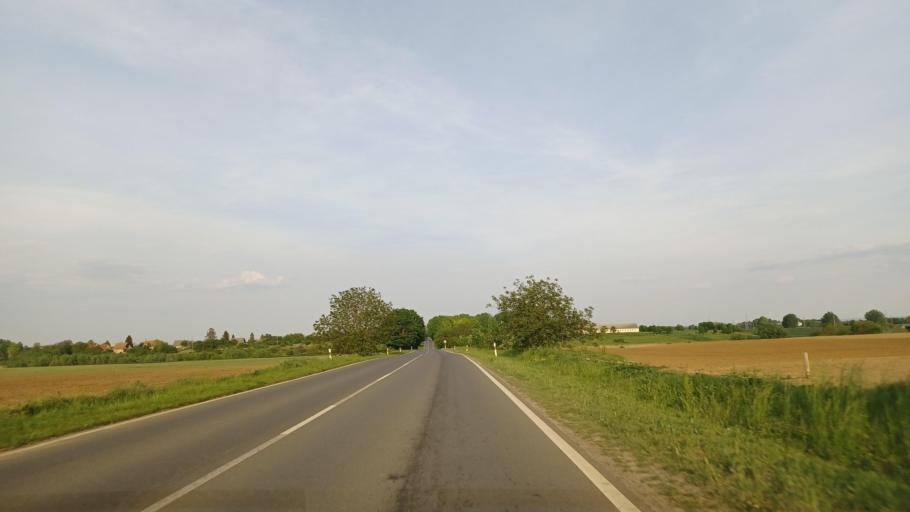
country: HU
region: Baranya
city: Boly
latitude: 45.9885
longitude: 18.5084
